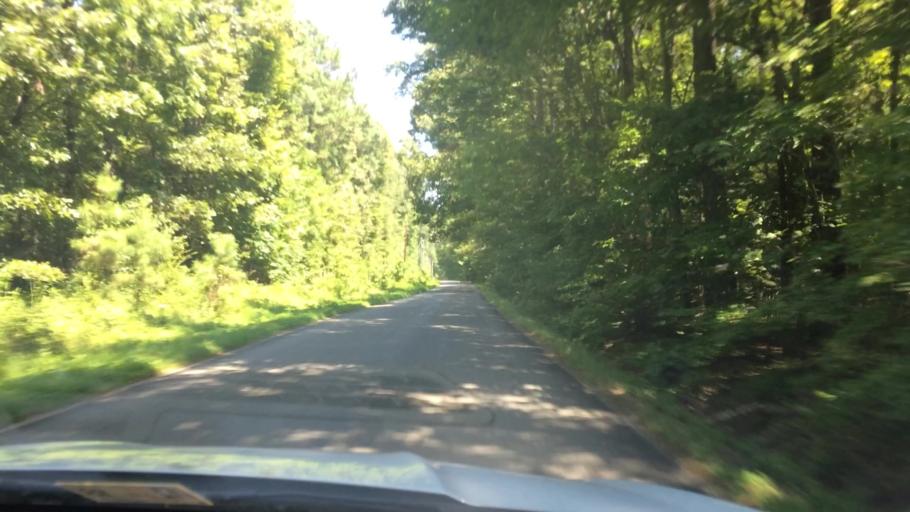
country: US
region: Virginia
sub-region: Charles City County
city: Charles City
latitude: 37.2673
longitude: -76.9459
